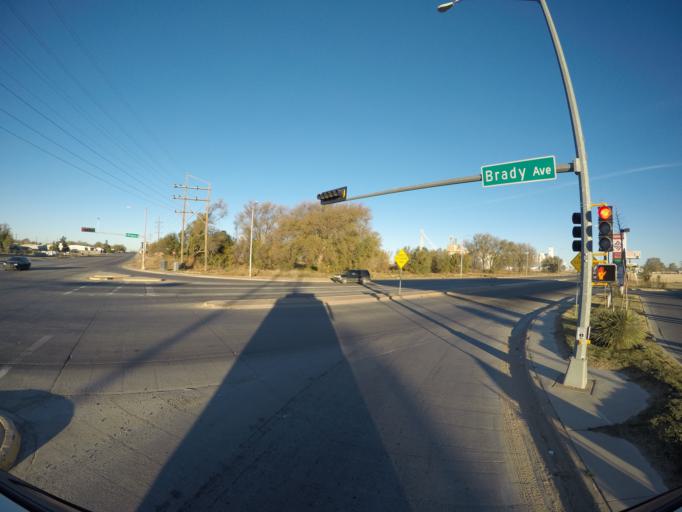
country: US
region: New Mexico
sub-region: Curry County
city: Clovis
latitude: 34.3904
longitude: -103.1963
